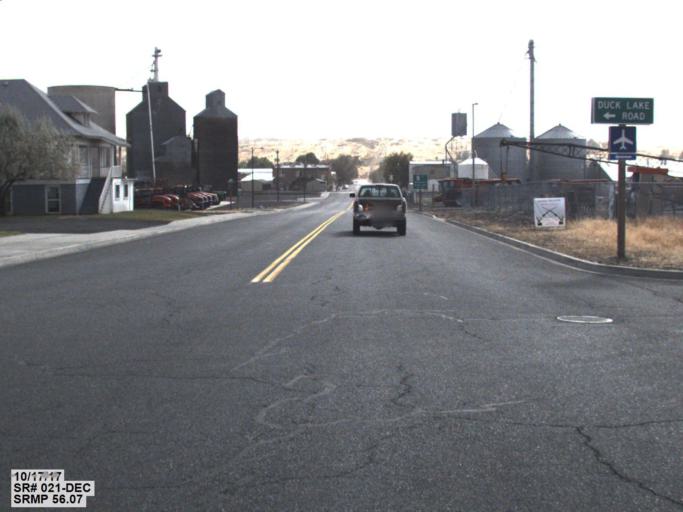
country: US
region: Washington
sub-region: Adams County
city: Ritzville
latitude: 47.3368
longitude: -118.6920
